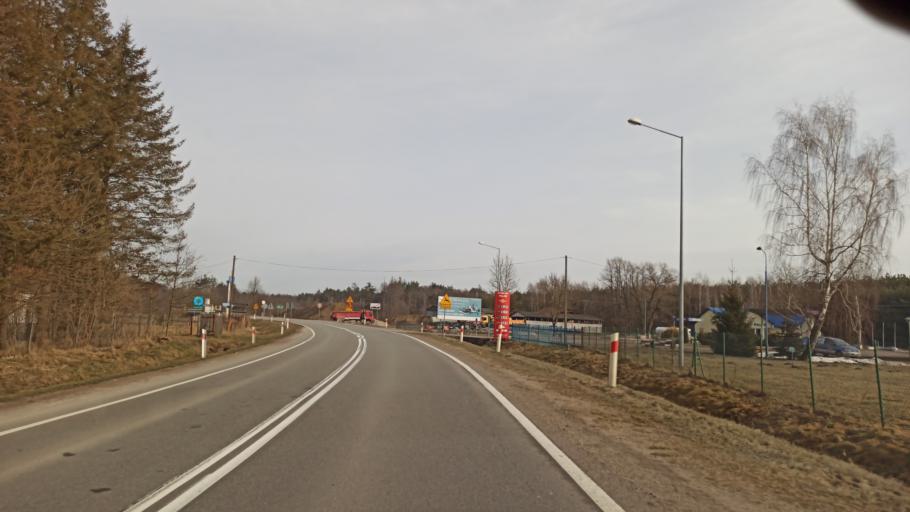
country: PL
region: Subcarpathian Voivodeship
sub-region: Powiat przeworski
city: Adamowka
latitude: 50.2942
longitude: 22.7207
